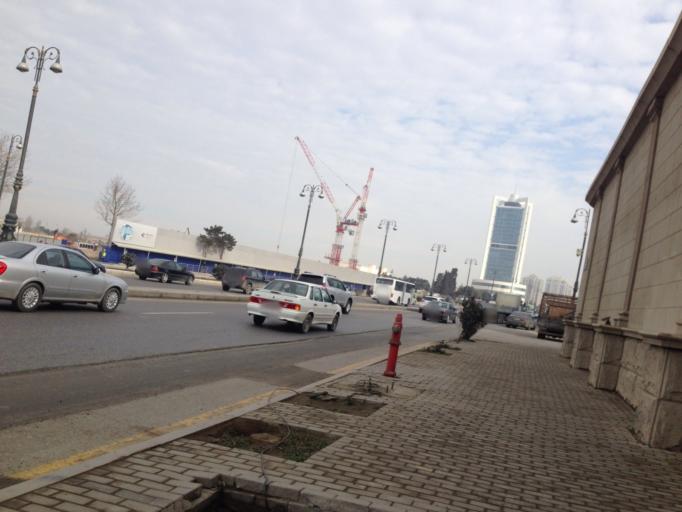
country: AZ
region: Baki
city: Baku
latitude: 40.4110
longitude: 49.8961
